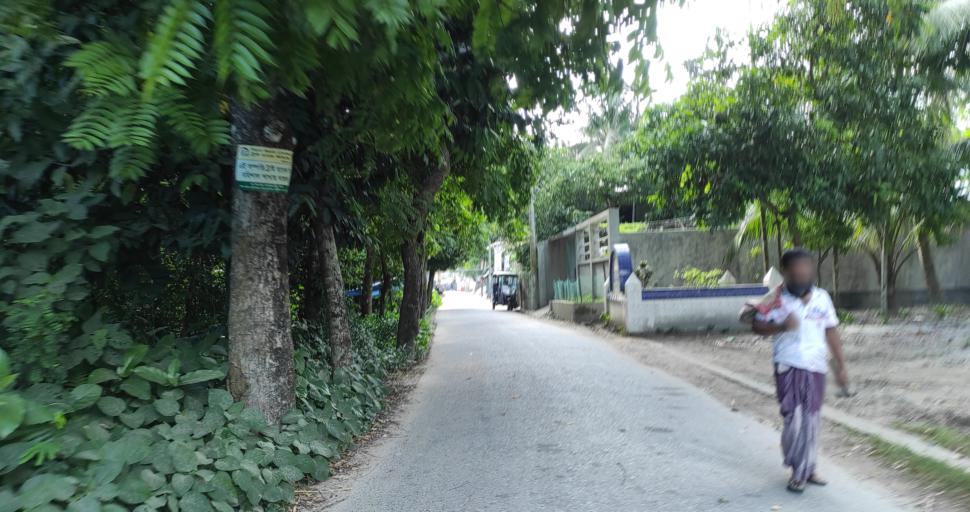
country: BD
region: Barisal
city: Gaurnadi
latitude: 22.8928
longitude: 90.1949
